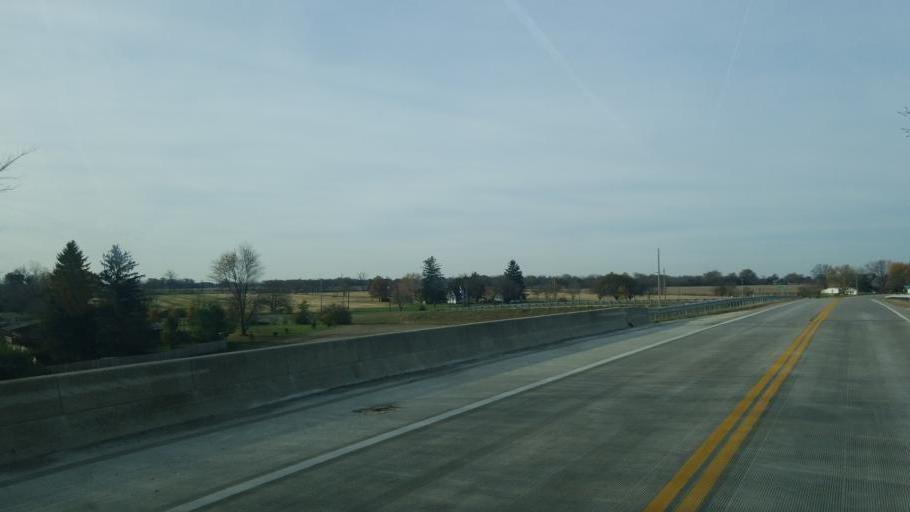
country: US
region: Ohio
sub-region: Madison County
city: Plain City
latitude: 40.1154
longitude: -83.2947
